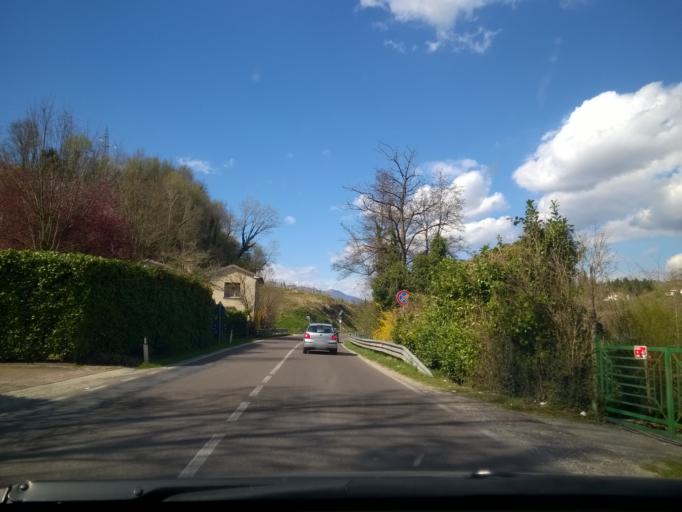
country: IT
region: Veneto
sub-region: Provincia di Treviso
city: San Pietro di Feletto
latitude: 45.8878
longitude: 12.2279
